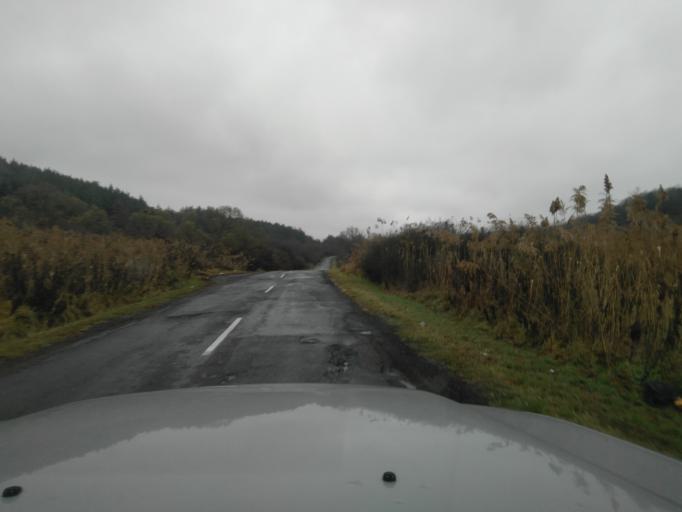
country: HU
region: Nograd
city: Kazar
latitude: 48.0198
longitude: 19.8618
